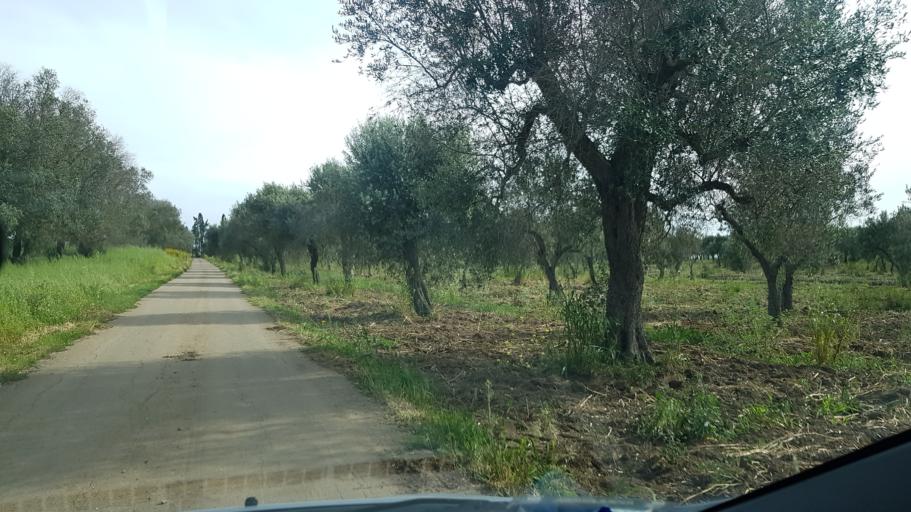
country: IT
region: Apulia
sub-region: Provincia di Brindisi
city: Tuturano
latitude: 40.5639
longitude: 17.9178
